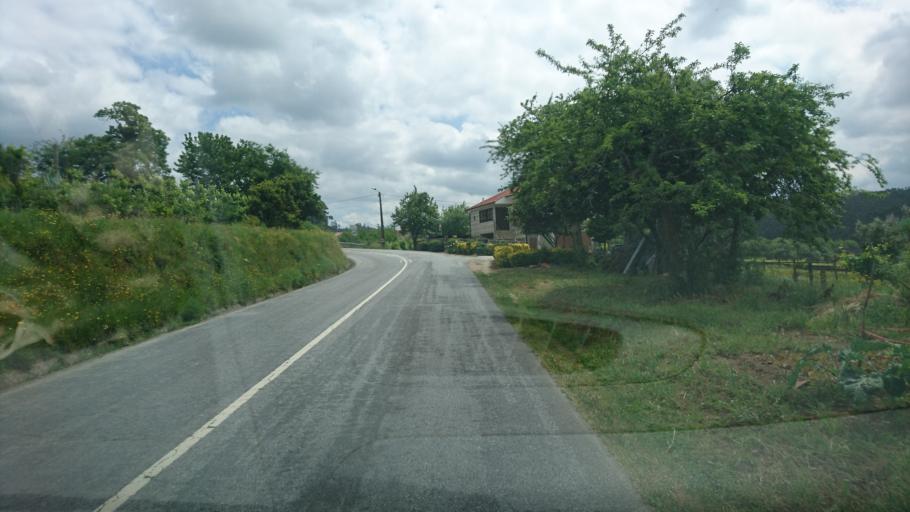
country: PT
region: Porto
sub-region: Paredes
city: Recarei
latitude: 41.1369
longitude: -8.3803
